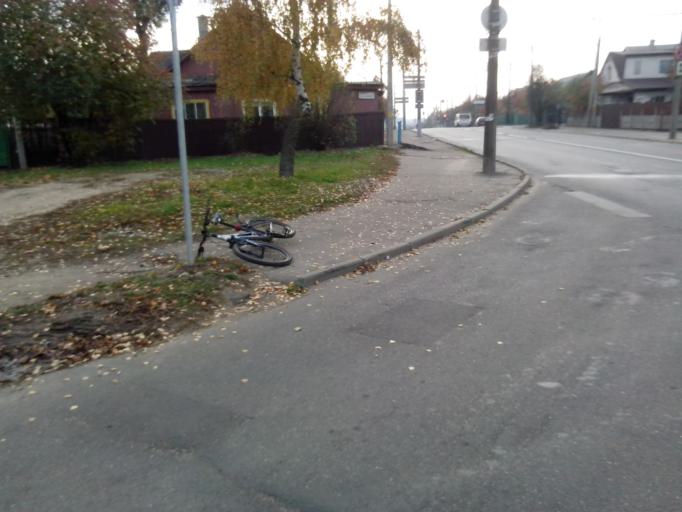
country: BY
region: Minsk
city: Minsk
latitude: 53.9474
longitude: 27.5947
